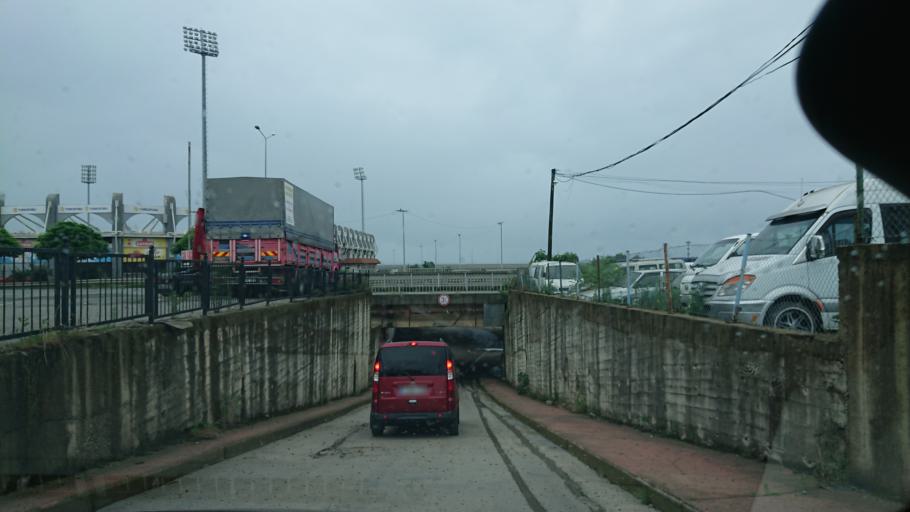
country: TR
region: Rize
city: Gundogdu
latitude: 41.0409
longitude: 40.5751
